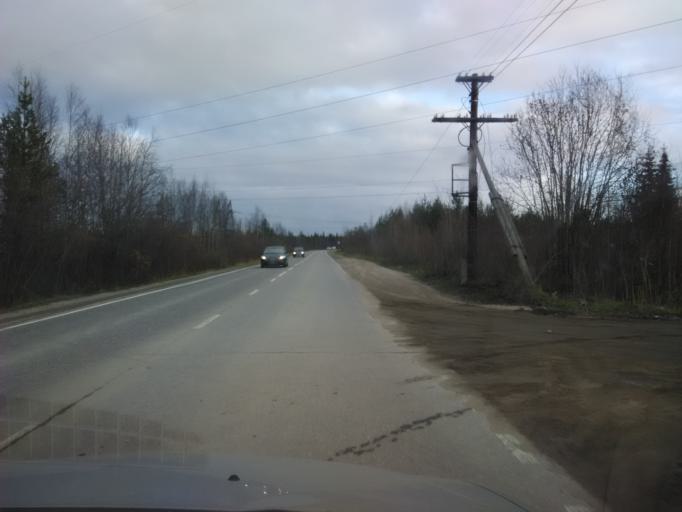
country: RU
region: Murmansk
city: Polyarnyye Zori
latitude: 67.3848
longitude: 32.5138
